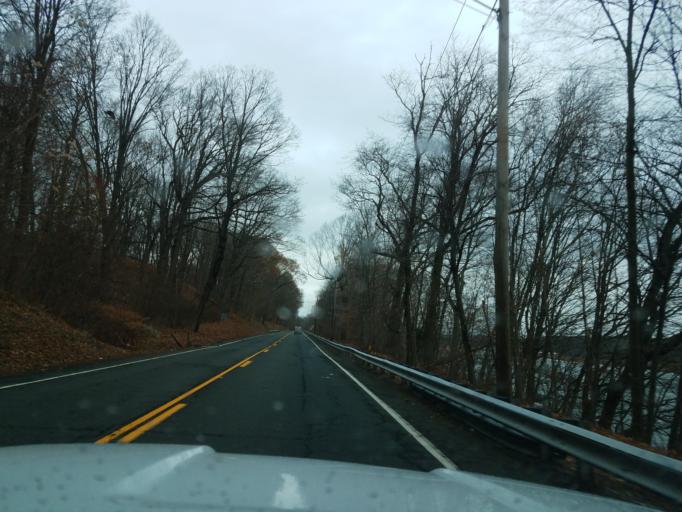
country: US
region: Connecticut
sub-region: New Haven County
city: City of Milford (balance)
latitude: 41.2334
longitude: -73.1090
